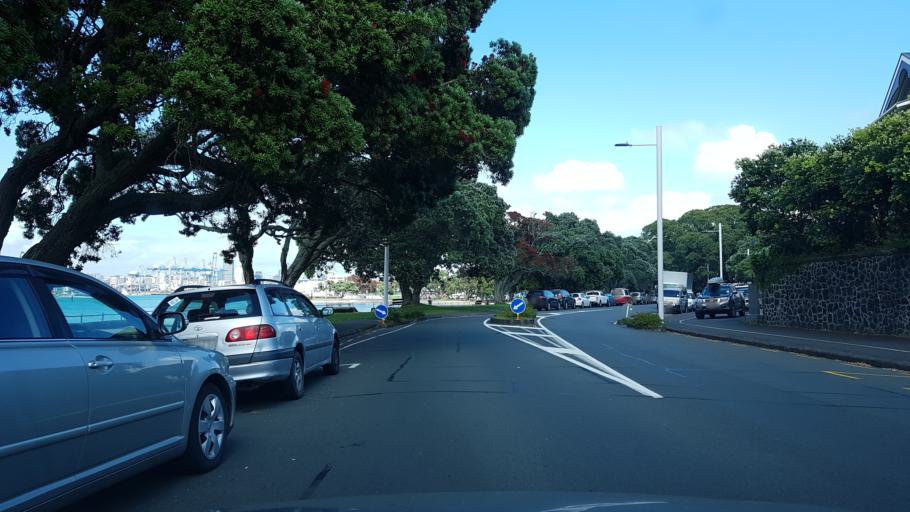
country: NZ
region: Auckland
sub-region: Auckland
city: Auckland
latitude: -36.8316
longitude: 174.8007
